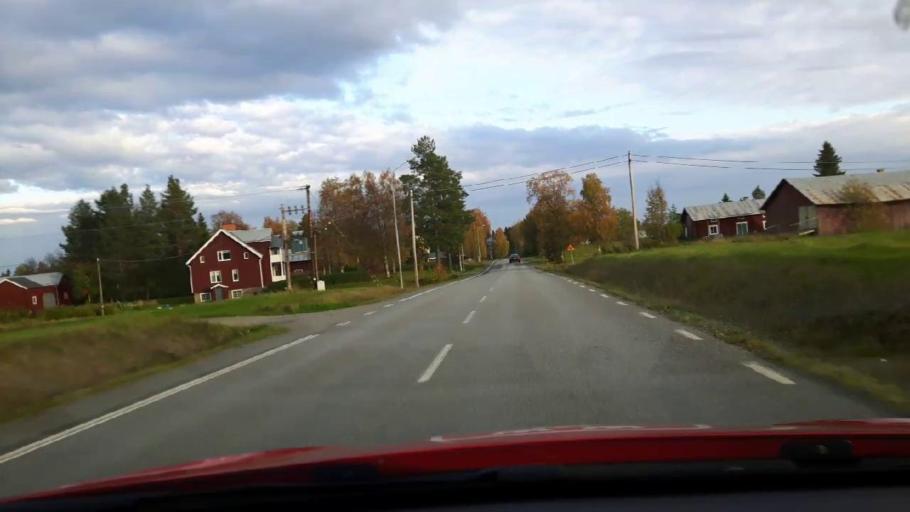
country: SE
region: Jaemtland
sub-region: Krokoms Kommun
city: Krokom
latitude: 63.3403
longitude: 14.5821
